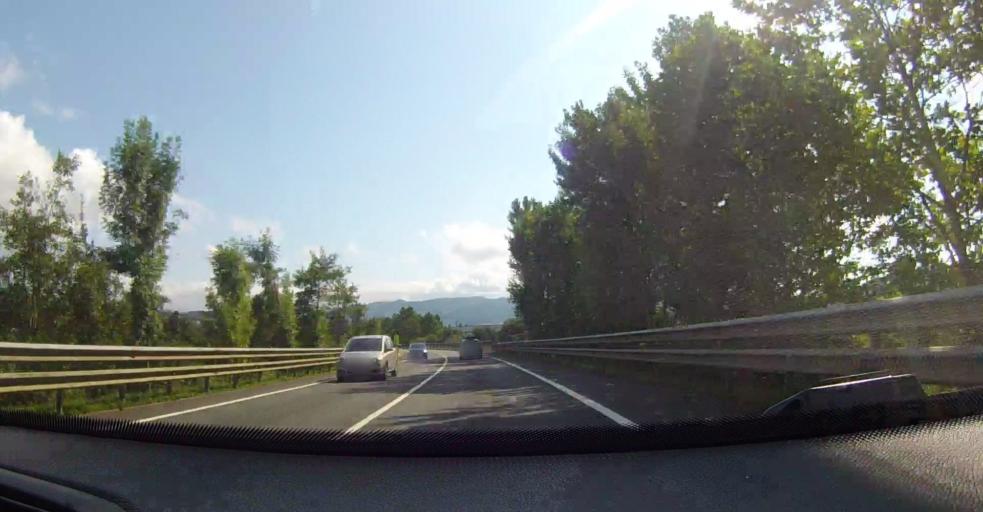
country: ES
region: Basque Country
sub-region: Bizkaia
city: Gernika-Lumo
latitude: 43.3153
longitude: -2.6706
